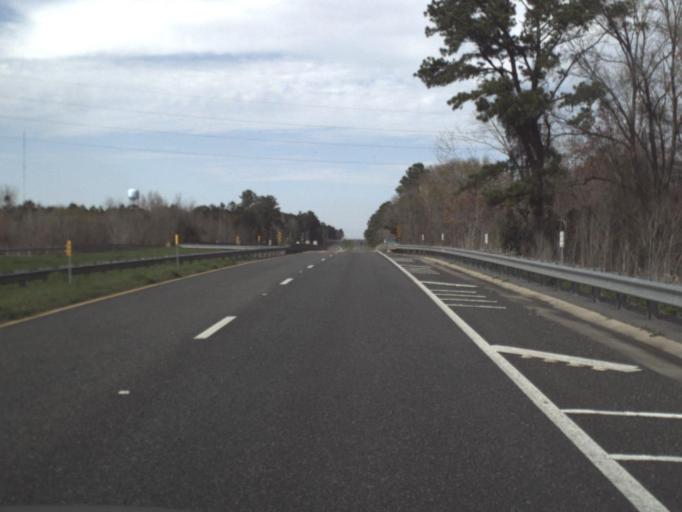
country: US
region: Florida
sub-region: Jefferson County
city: Monticello
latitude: 30.4950
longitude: -83.8806
